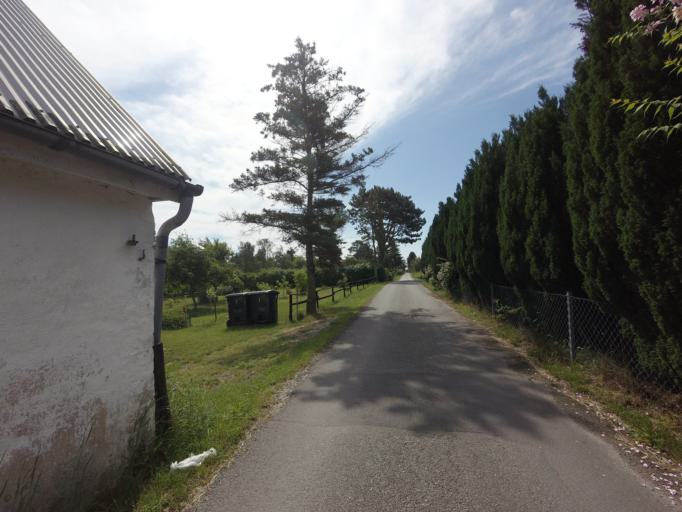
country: SE
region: Skane
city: Smygehamn
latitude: 55.3581
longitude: 13.4200
